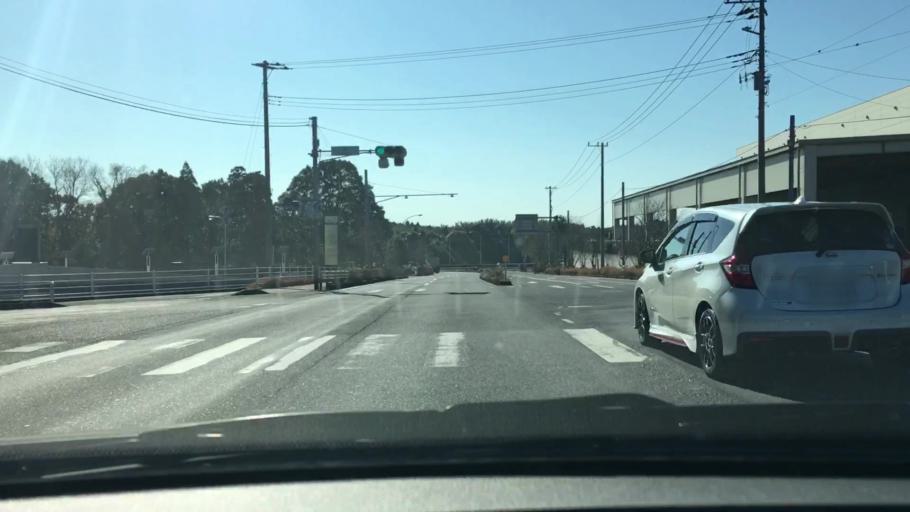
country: JP
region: Chiba
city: Narita
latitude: 35.7408
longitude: 140.4021
